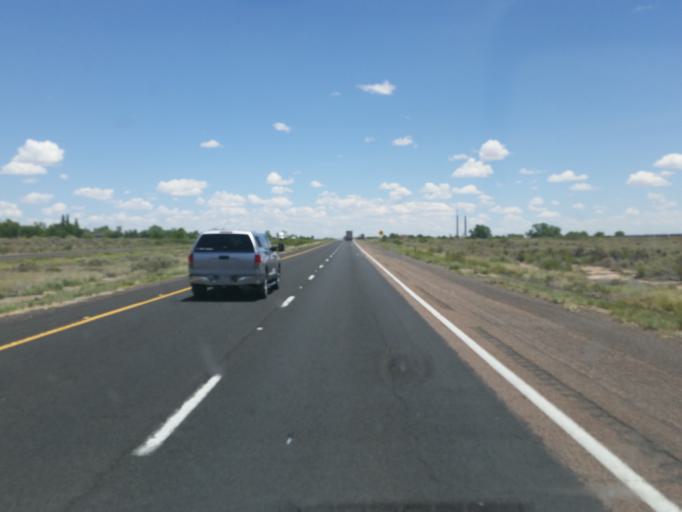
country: US
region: Arizona
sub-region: Navajo County
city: Joseph City
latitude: 34.9560
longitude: -110.3510
